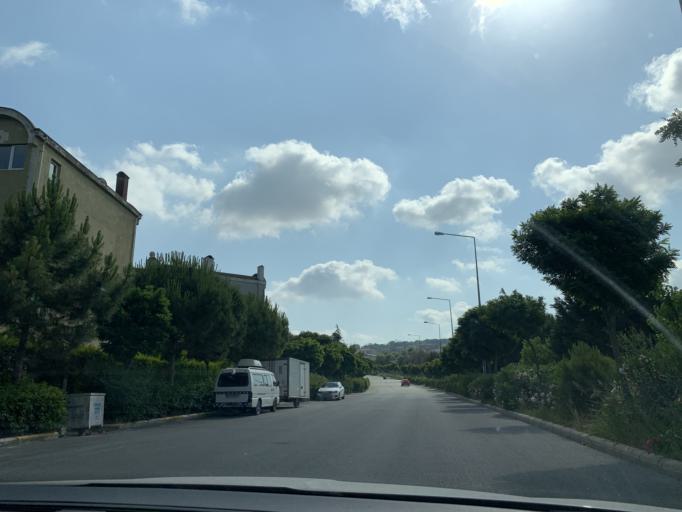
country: TR
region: Istanbul
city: Esenyurt
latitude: 41.0844
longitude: 28.6715
